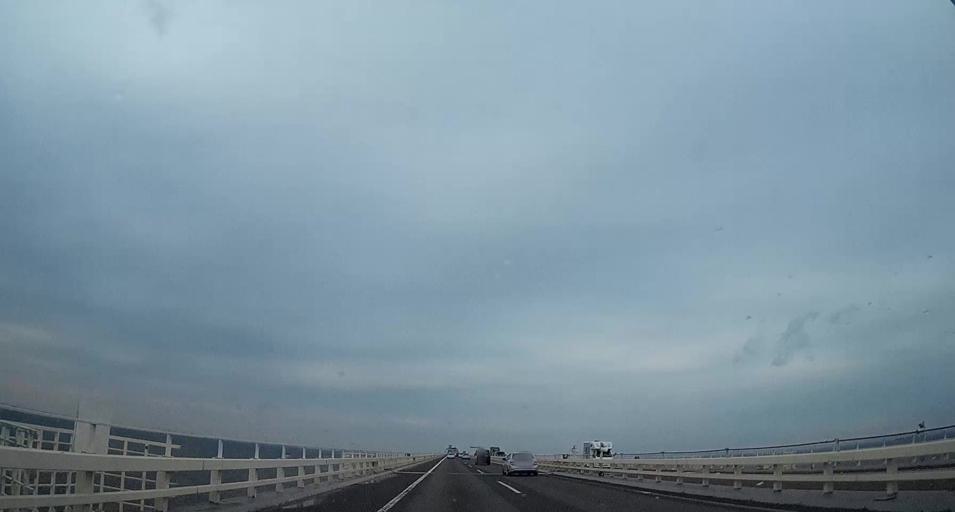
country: JP
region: Chiba
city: Kisarazu
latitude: 35.4447
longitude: 139.9032
